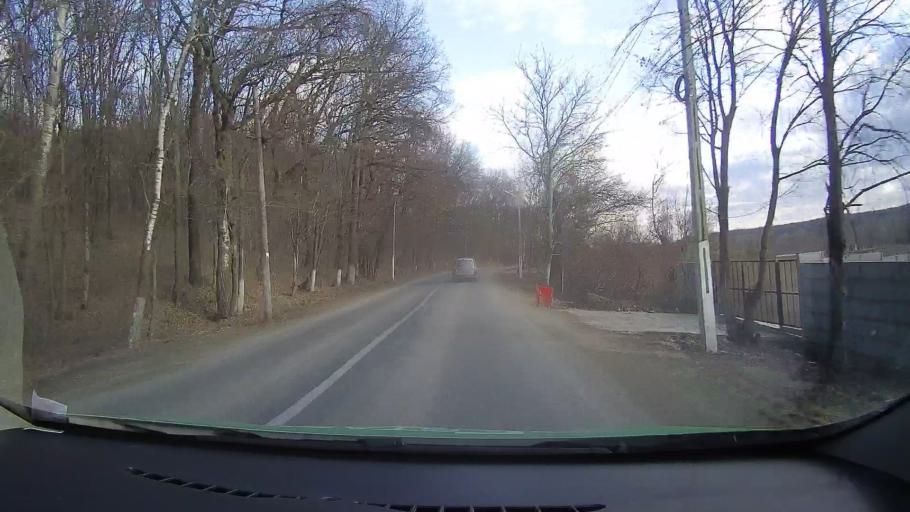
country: RO
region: Dambovita
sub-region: Comuna Gura Ocnitei
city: Gura Ocnitei
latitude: 44.9554
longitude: 25.5528
